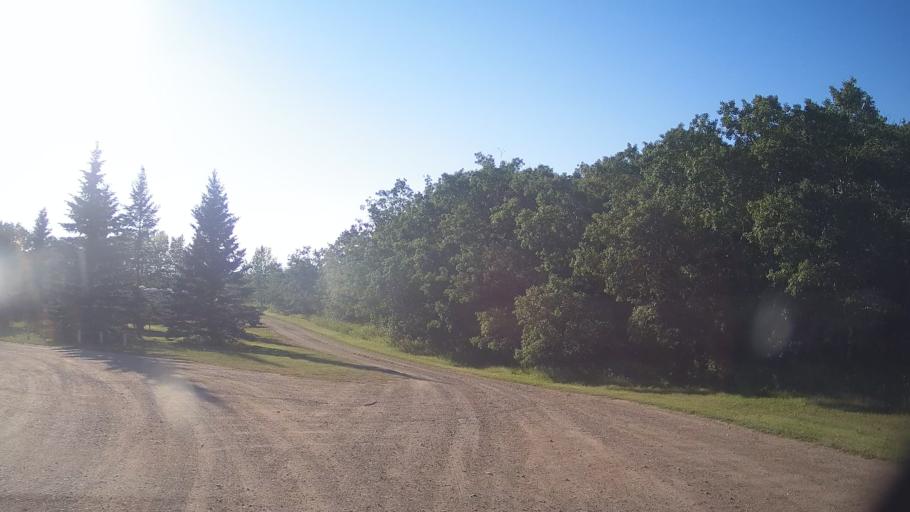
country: CA
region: Saskatchewan
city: Lanigan
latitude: 51.8511
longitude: -105.0181
